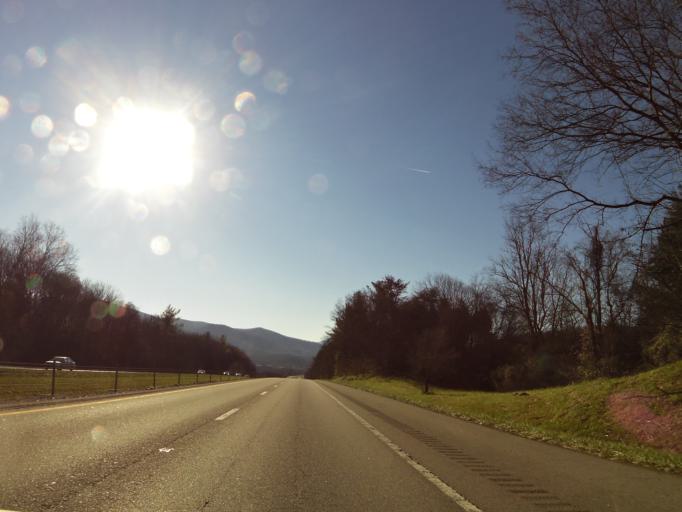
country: US
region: Tennessee
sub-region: Cocke County
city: Newport
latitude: 35.9153
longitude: -83.1873
